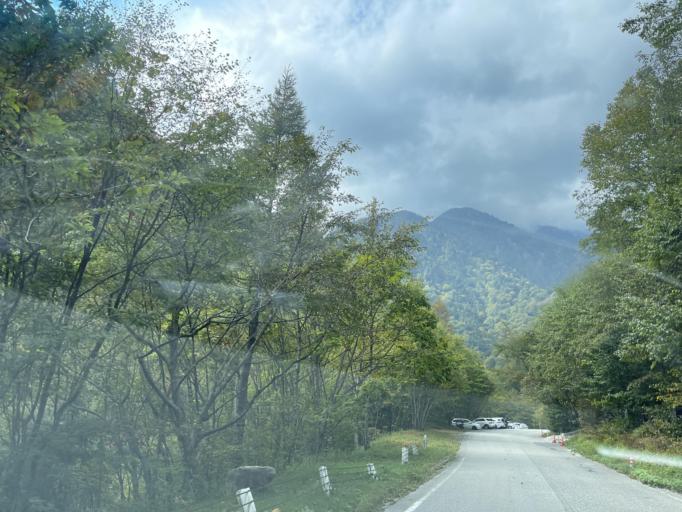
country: JP
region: Nagano
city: Omachi
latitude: 36.4936
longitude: 137.7261
